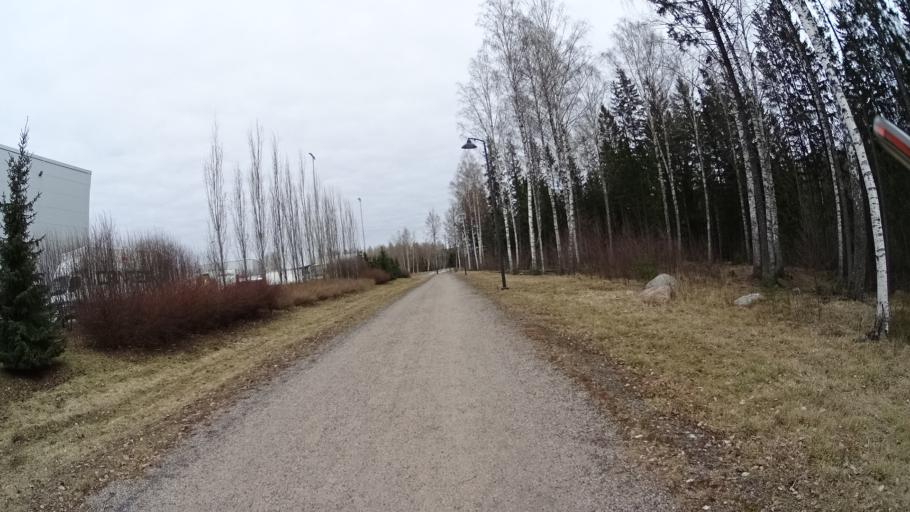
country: FI
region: Uusimaa
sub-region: Helsinki
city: Vantaa
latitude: 60.2982
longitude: 24.9352
